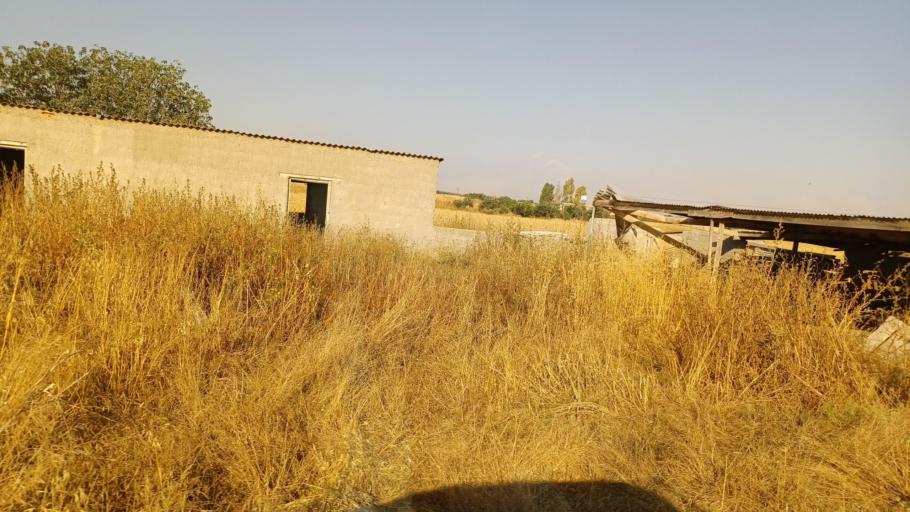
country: CY
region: Ammochostos
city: Acheritou
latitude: 35.1013
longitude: 33.8817
